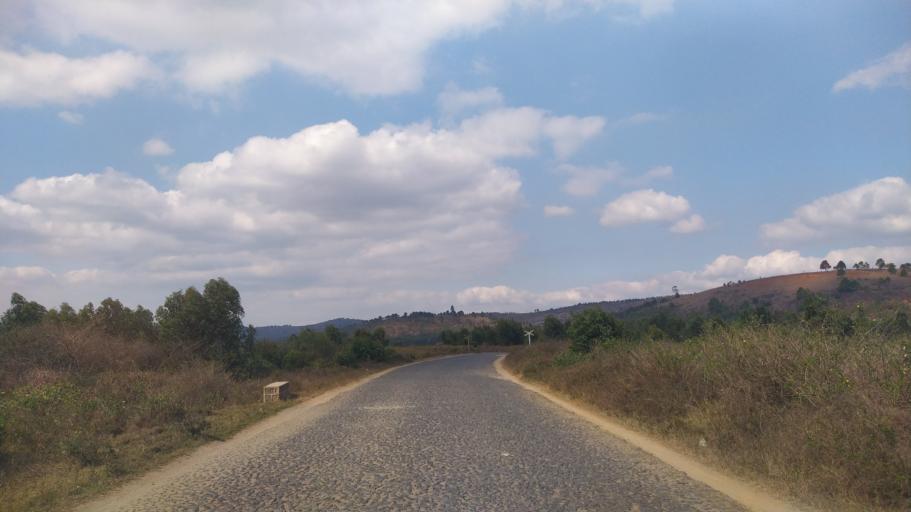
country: MG
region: Alaotra Mangoro
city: Moramanga
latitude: -18.7682
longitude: 48.2524
